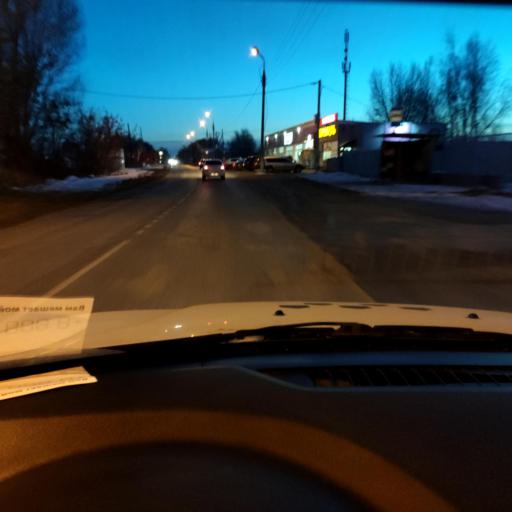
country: RU
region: Samara
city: Tol'yatti
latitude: 53.5576
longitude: 49.3942
